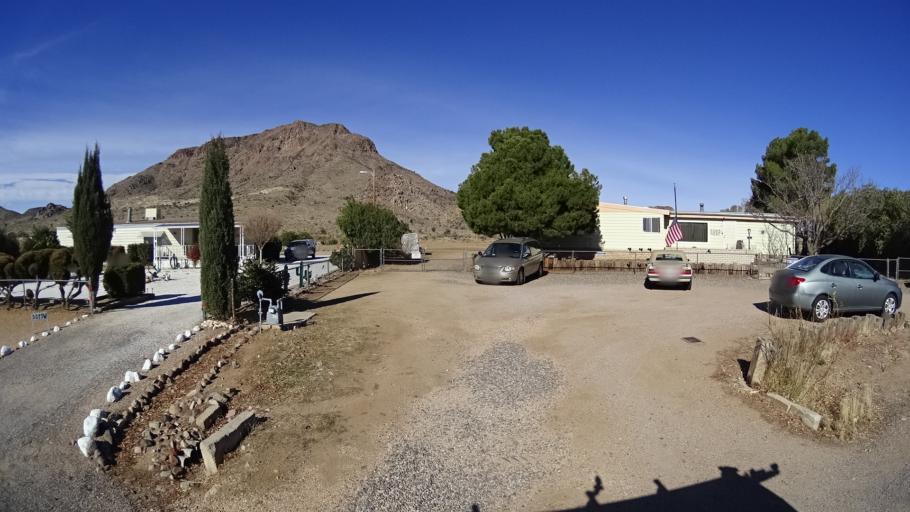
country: US
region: Arizona
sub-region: Mohave County
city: New Kingman-Butler
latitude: 35.2725
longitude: -114.0490
